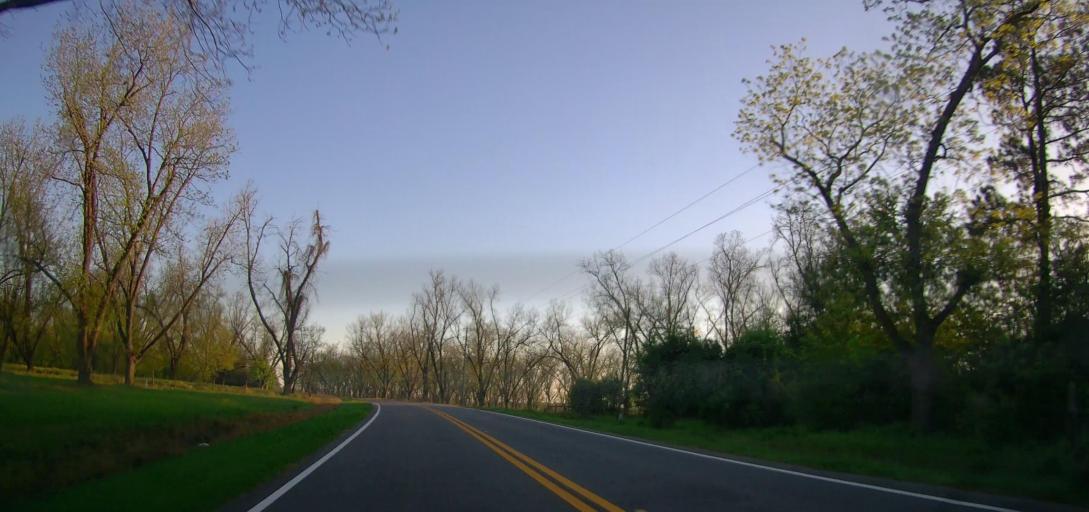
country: US
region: Georgia
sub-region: Irwin County
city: Ocilla
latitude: 31.6379
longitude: -83.2751
